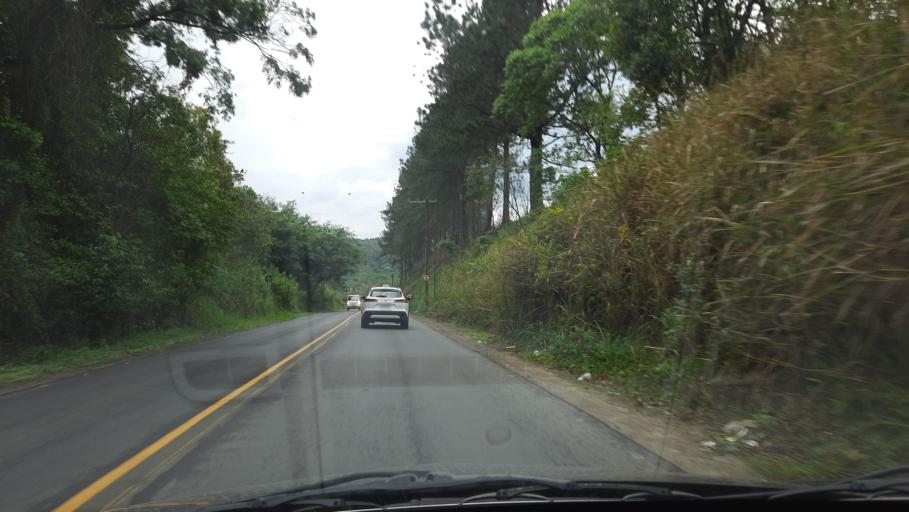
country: BR
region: Sao Paulo
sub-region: Caieiras
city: Caieiras
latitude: -23.3684
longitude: -46.6672
